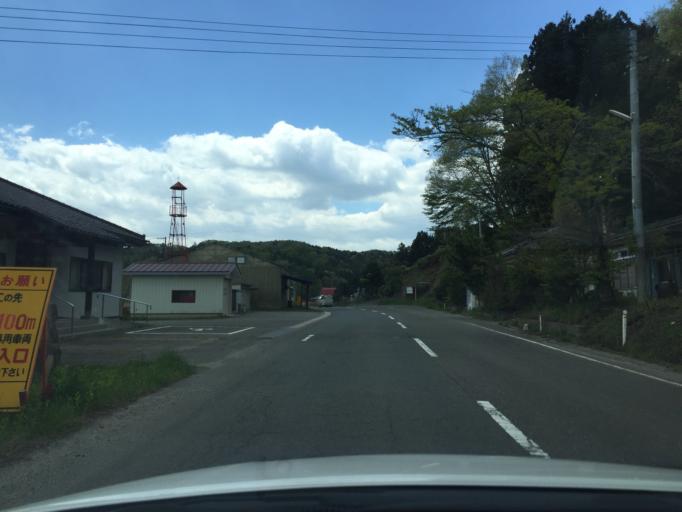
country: JP
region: Fukushima
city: Yanagawamachi-saiwaicho
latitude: 37.7169
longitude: 140.6912
